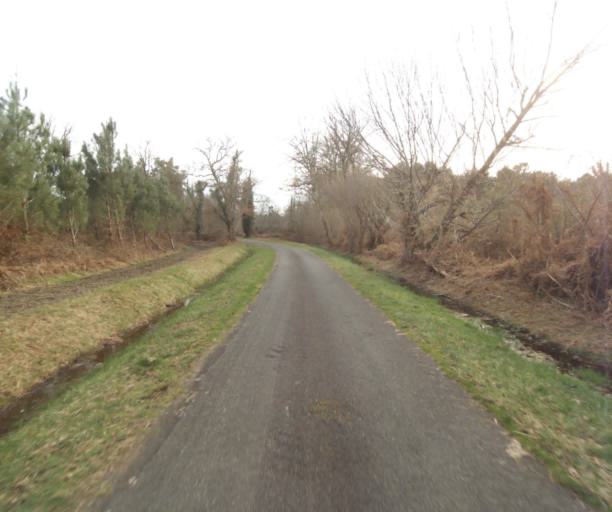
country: FR
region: Aquitaine
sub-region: Departement des Landes
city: Gabarret
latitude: 44.0121
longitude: 0.0440
